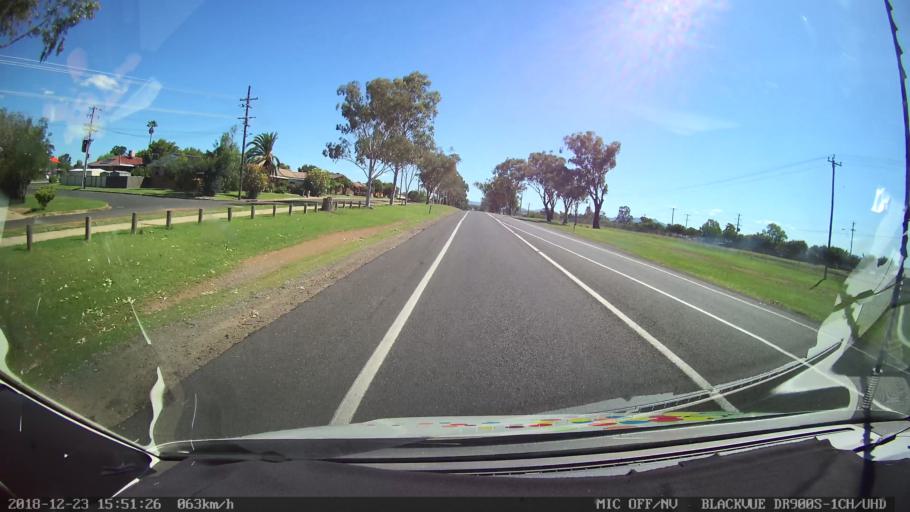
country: AU
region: New South Wales
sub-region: Tamworth Municipality
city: South Tamworth
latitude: -31.1127
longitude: 150.8959
